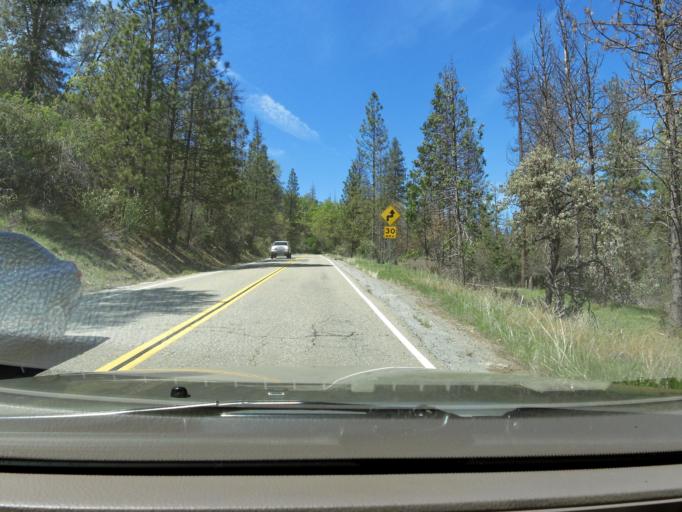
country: US
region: California
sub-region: Madera County
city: Oakhurst
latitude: 37.2612
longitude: -119.5719
